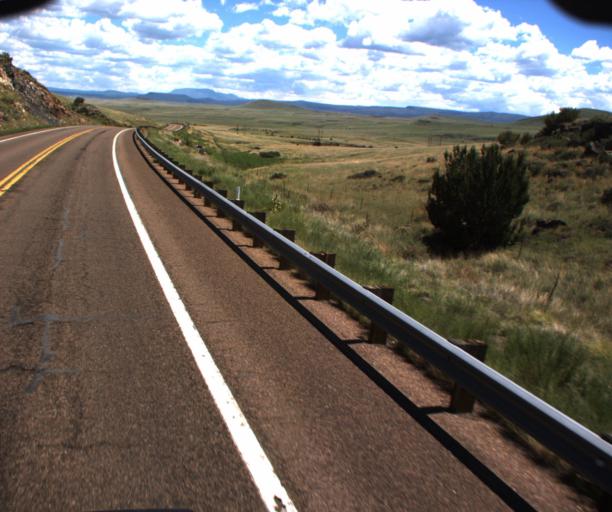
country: US
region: Arizona
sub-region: Apache County
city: Springerville
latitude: 34.2112
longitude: -109.4278
